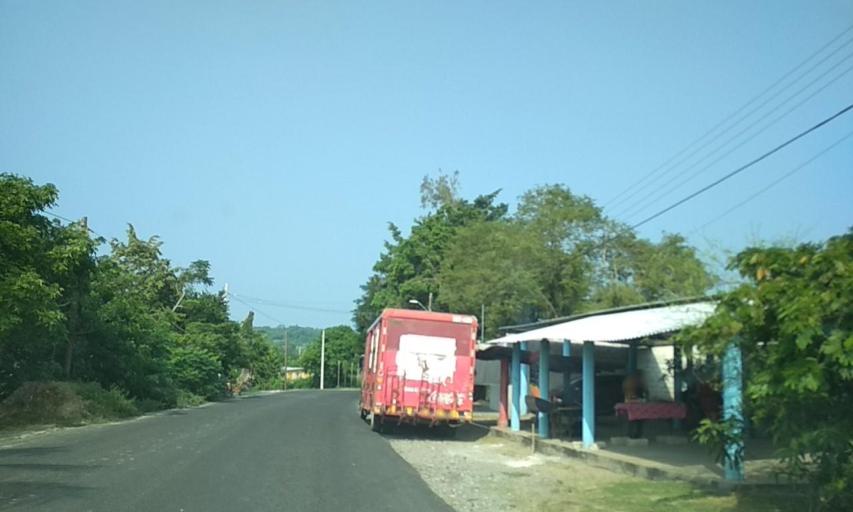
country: MX
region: Veracruz
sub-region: Misantla
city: La Defensa
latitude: 20.0514
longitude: -96.9890
